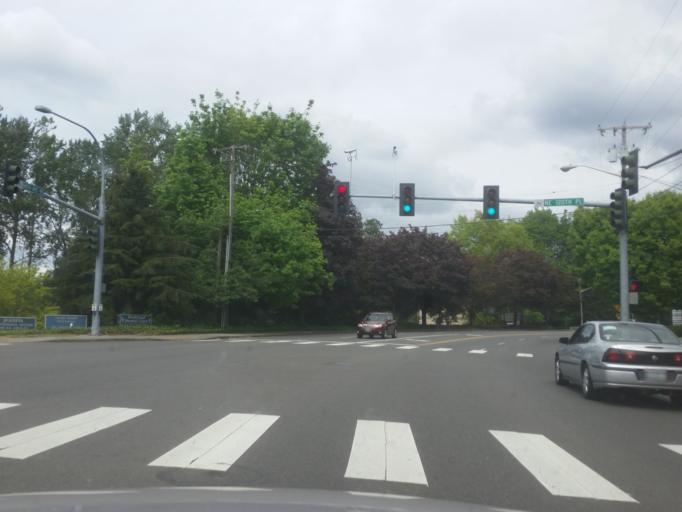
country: US
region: Washington
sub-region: King County
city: Inglewood-Finn Hill
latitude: 47.7080
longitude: -122.2104
